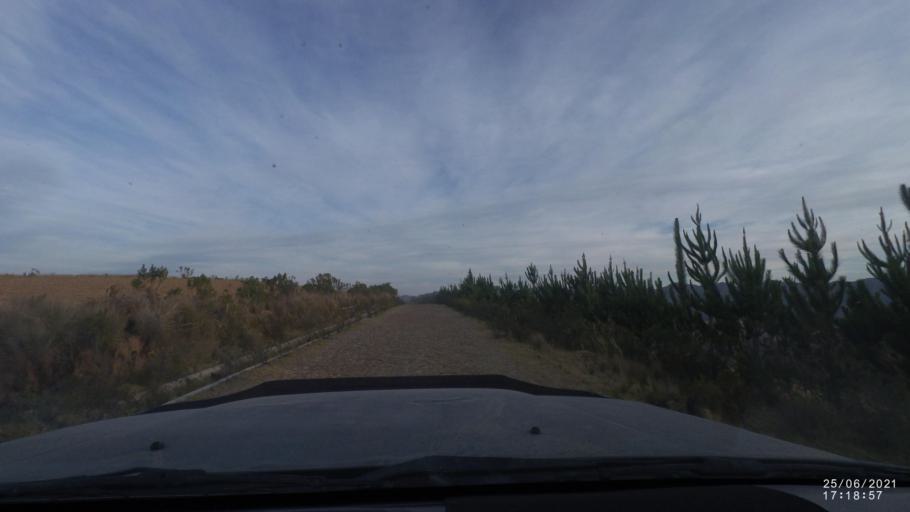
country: BO
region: Cochabamba
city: Arani
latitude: -17.8976
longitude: -65.6925
